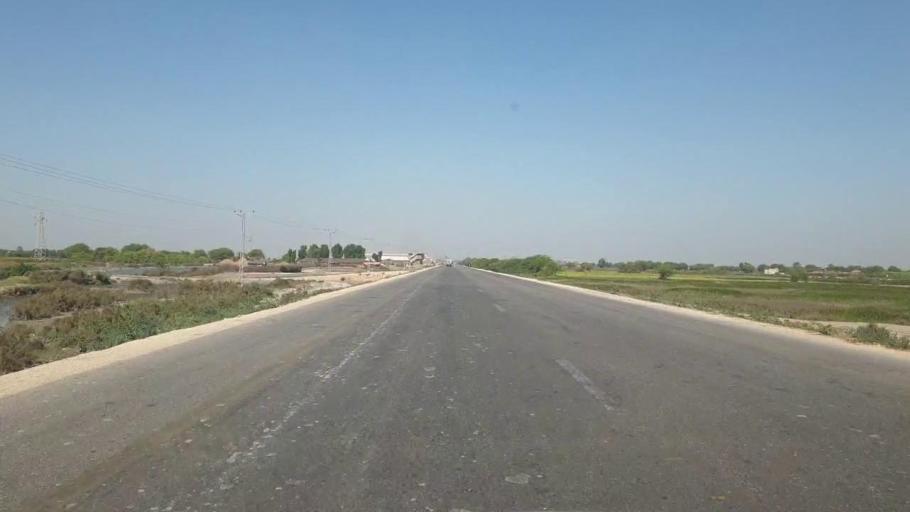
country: PK
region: Sindh
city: Talhar
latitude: 24.8587
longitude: 68.8166
